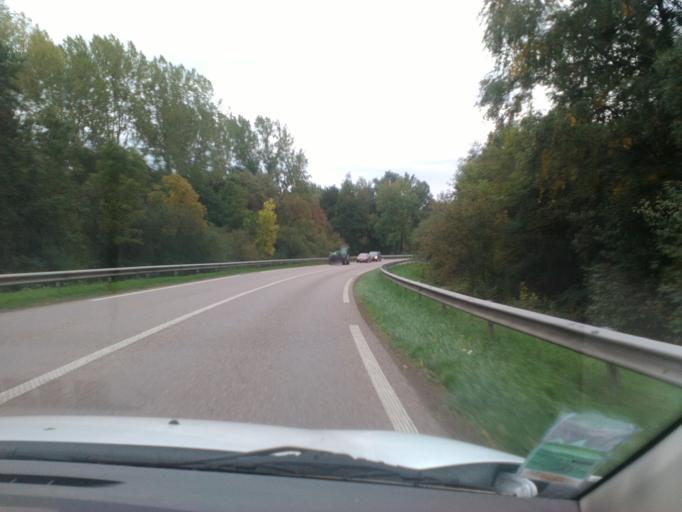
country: FR
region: Lorraine
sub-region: Departement des Vosges
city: Rambervillers
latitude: 48.3357
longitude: 6.6521
